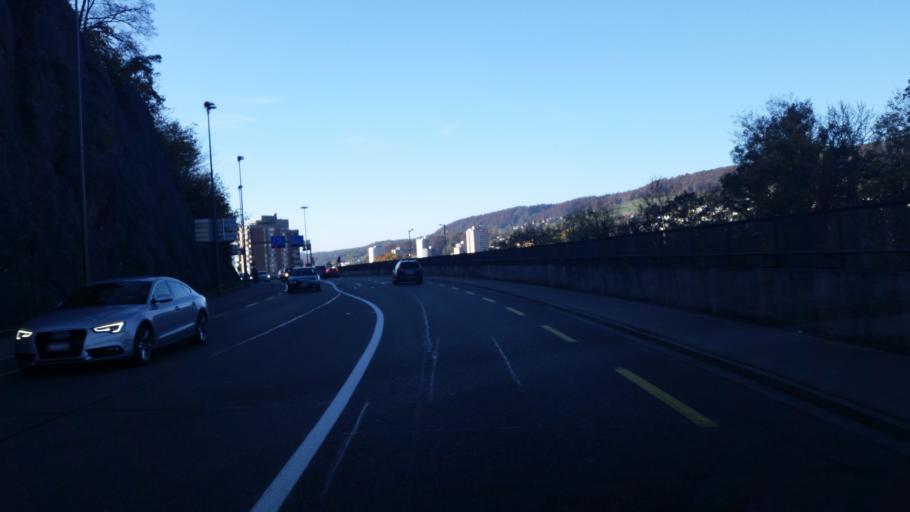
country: CH
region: Aargau
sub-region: Bezirk Baden
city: Obersiggenthal
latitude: 47.4819
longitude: 8.3000
